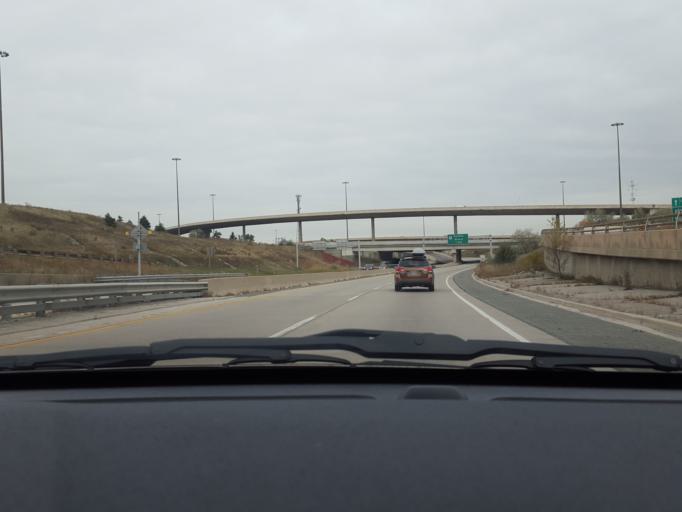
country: CA
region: Ontario
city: Etobicoke
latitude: 43.6110
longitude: -79.5489
